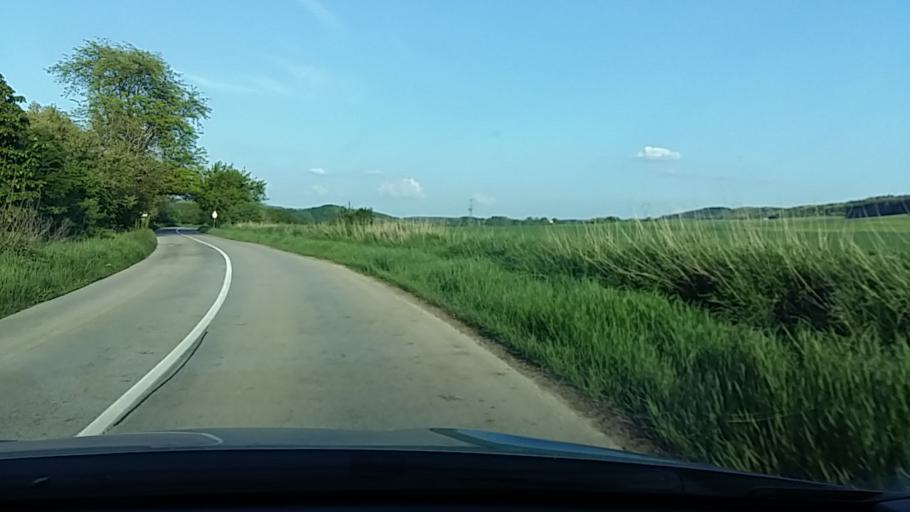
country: HU
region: Pest
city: Szod
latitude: 47.7564
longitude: 19.1902
